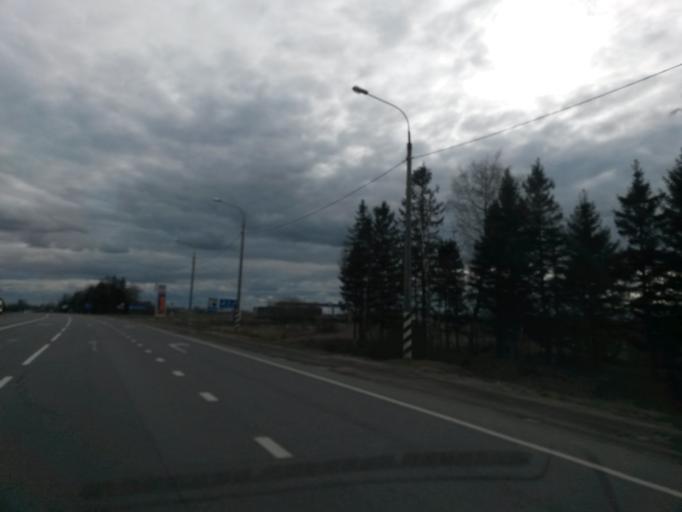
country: RU
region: Jaroslavl
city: Semibratovo
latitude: 57.3697
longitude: 39.6009
